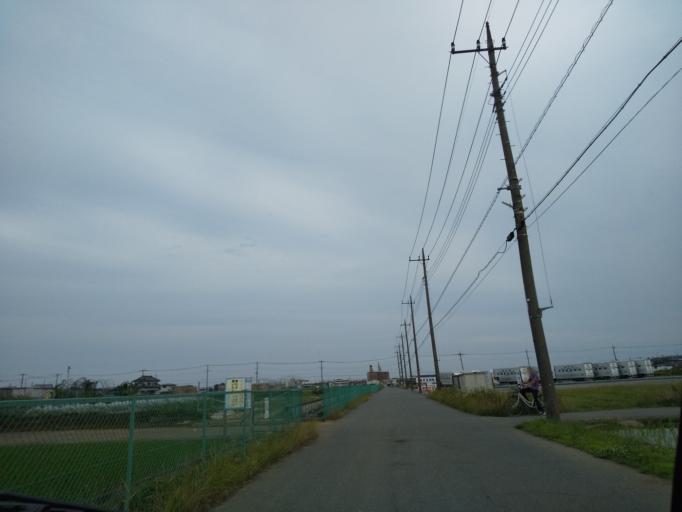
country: JP
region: Kanagawa
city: Zama
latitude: 35.4750
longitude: 139.3560
